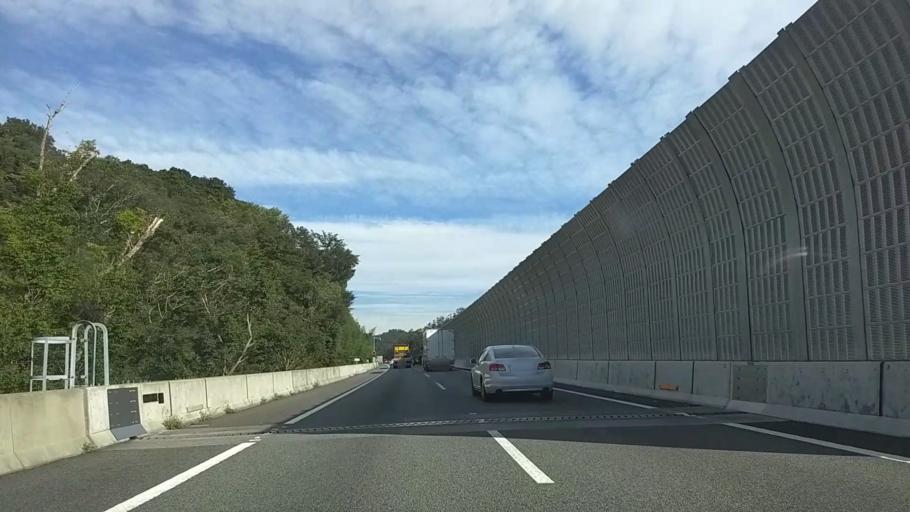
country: JP
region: Kanagawa
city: Zama
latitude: 35.5501
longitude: 139.3182
